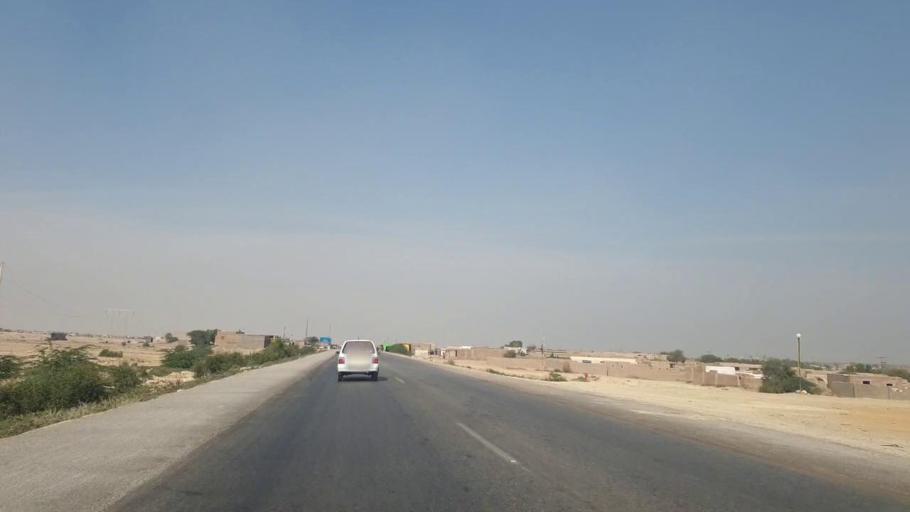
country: PK
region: Sindh
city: Hala
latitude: 25.7905
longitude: 68.2815
